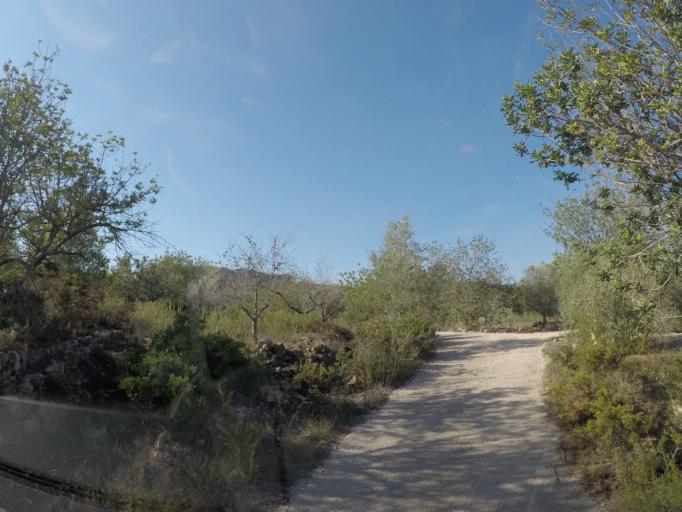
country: ES
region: Catalonia
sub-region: Provincia de Tarragona
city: El Perello
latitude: 40.9184
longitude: 0.7230
